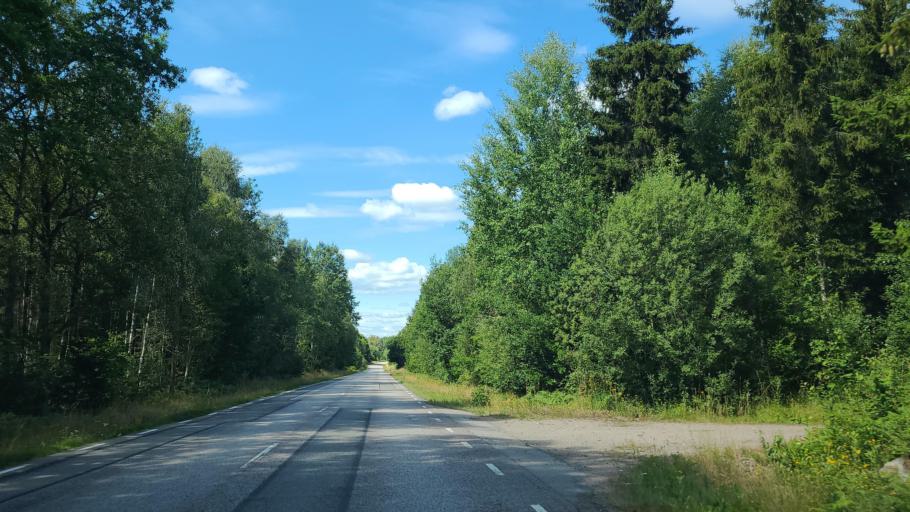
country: SE
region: Kalmar
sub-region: Emmaboda Kommun
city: Emmaboda
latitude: 56.5337
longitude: 15.6309
